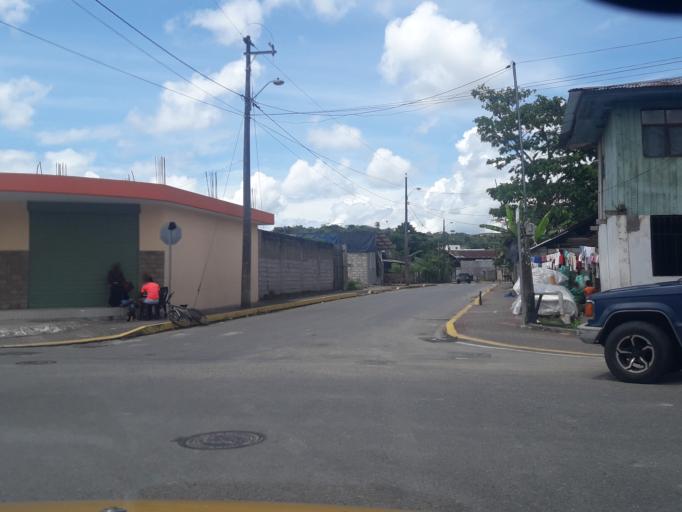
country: EC
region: Napo
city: Tena
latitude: -1.0059
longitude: -77.8194
